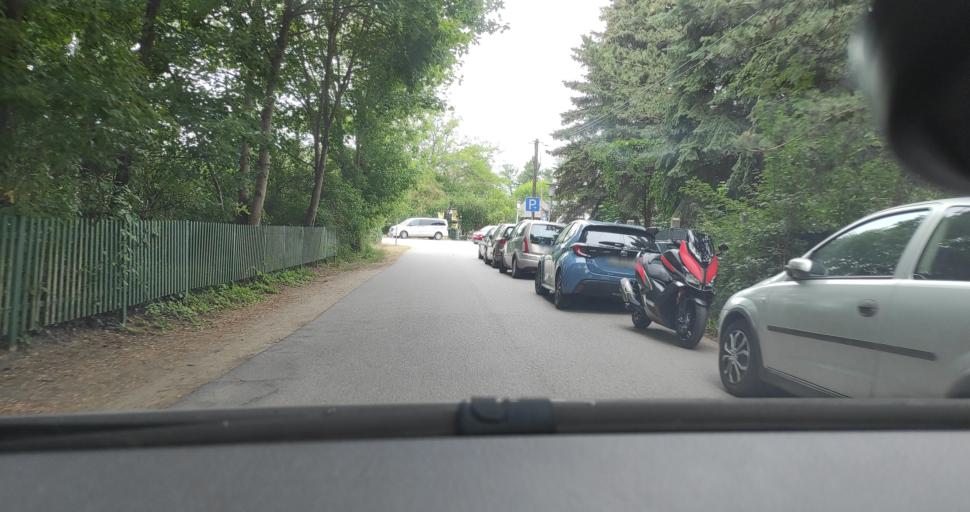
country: DE
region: Brandenburg
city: Neu Zauche
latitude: 52.0143
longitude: 14.1831
